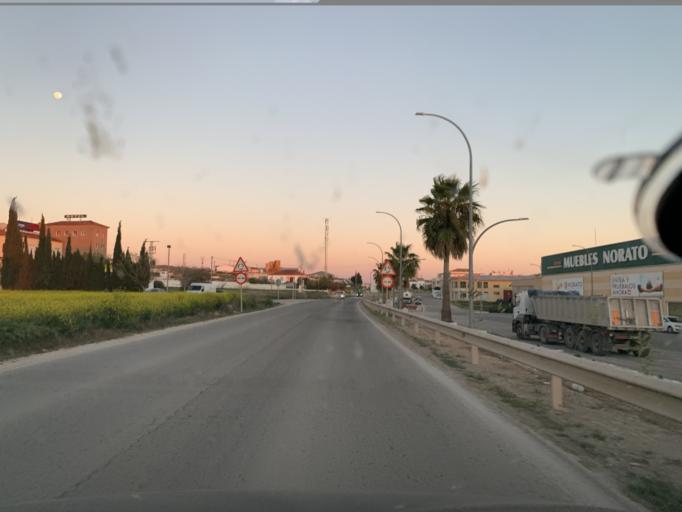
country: ES
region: Andalusia
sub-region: Provincia de Sevilla
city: Pedrera
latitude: 37.2333
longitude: -4.9013
